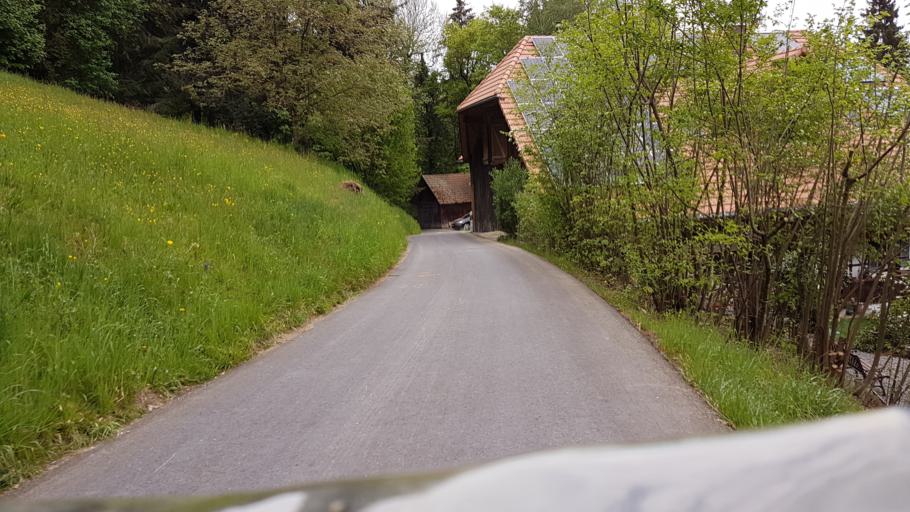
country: CH
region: Bern
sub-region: Bern-Mittelland District
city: Munsingen
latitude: 46.8651
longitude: 7.5455
